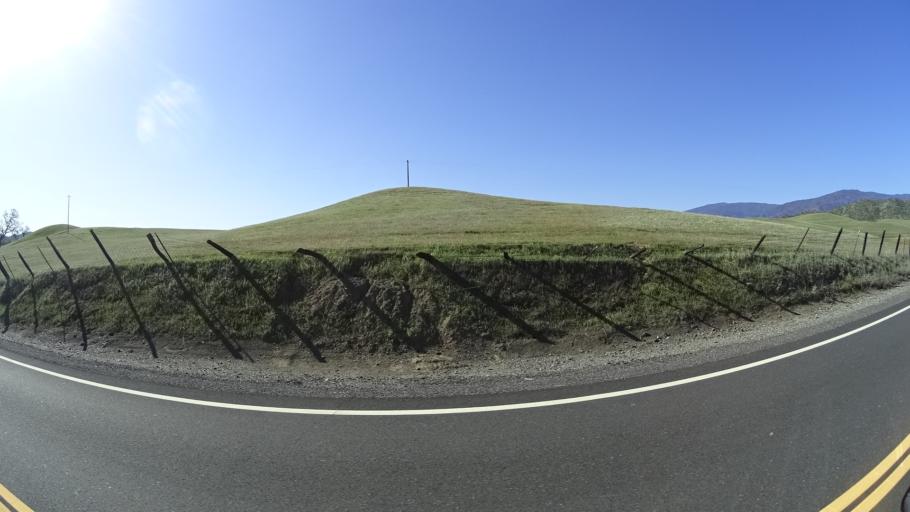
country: US
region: California
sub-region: Glenn County
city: Orland
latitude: 39.6594
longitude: -122.5479
